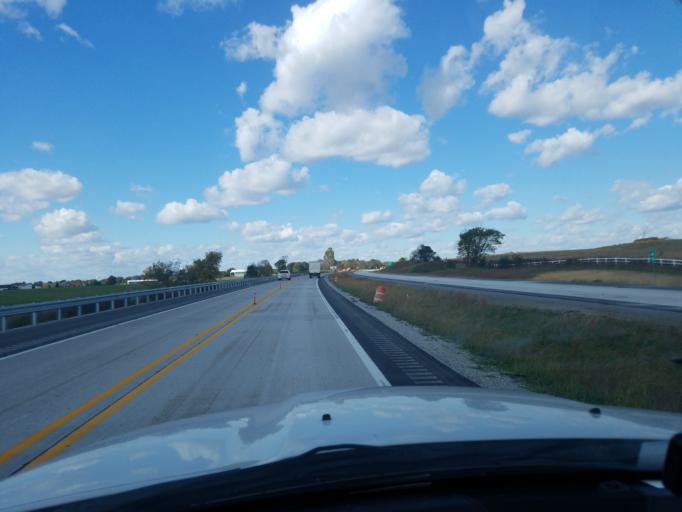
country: US
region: Kentucky
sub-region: Ohio County
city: Hartford
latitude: 37.4482
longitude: -86.8711
